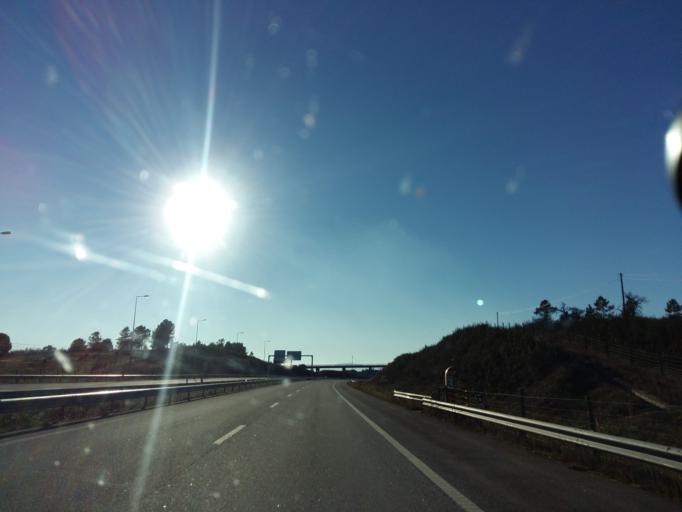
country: PT
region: Castelo Branco
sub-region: Castelo Branco
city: Castelo Branco
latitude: 39.7580
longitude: -7.6089
